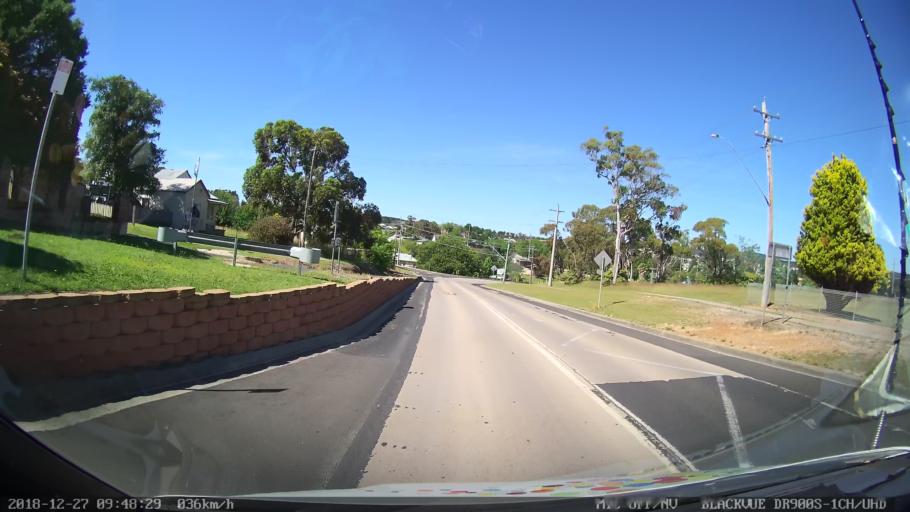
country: AU
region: New South Wales
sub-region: Lithgow
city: Portland
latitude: -33.3529
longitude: 149.9881
